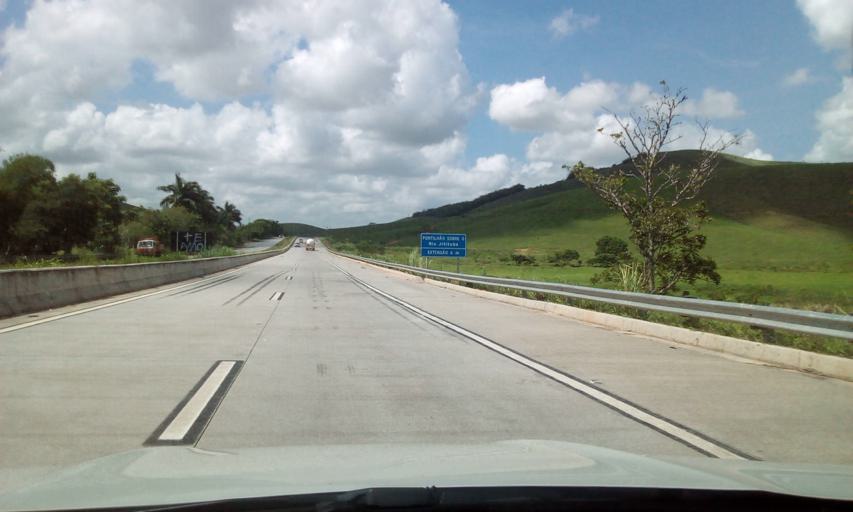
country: BR
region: Alagoas
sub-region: Flexeiras
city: Flexeiras
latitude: -9.2566
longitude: -35.7746
